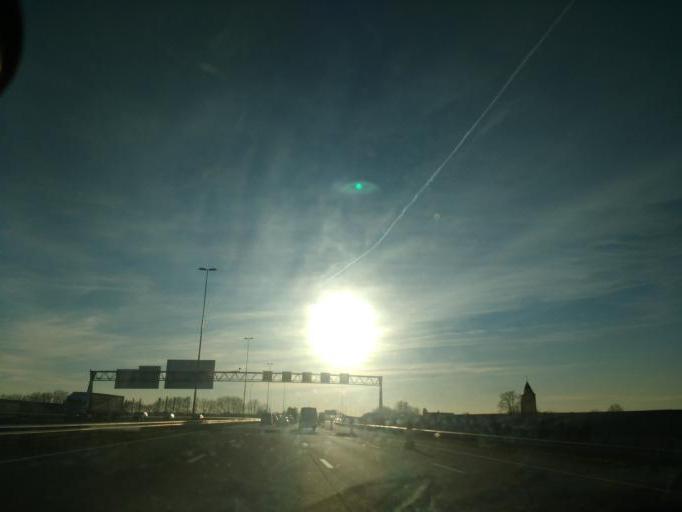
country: NL
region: Gelderland
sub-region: Gemeente Overbetuwe
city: Herveld
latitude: 51.8993
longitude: 5.7550
